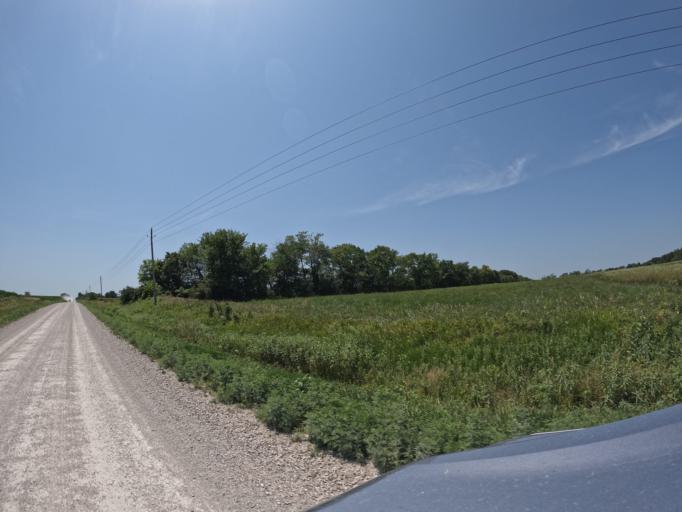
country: US
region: Iowa
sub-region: Henry County
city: Mount Pleasant
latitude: 40.9199
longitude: -91.6460
